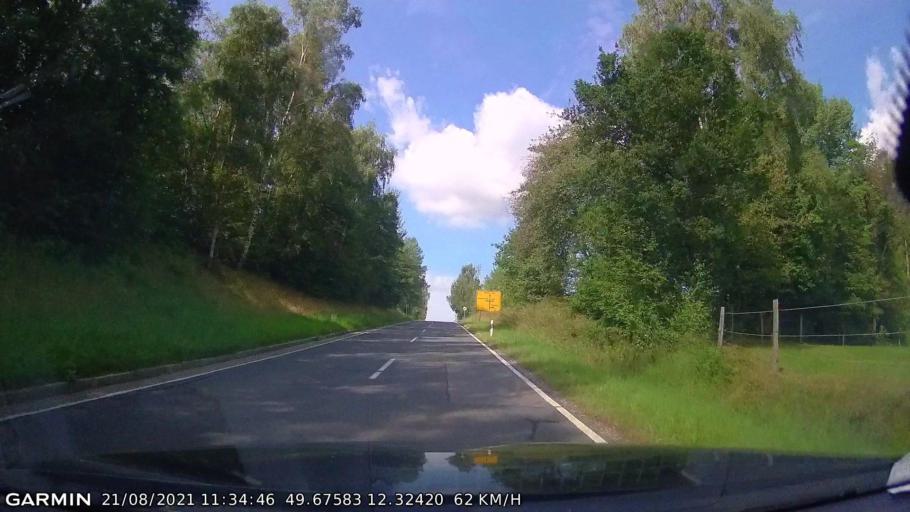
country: DE
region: Bavaria
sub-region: Upper Palatinate
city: Waldthurn
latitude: 49.6759
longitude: 12.3240
